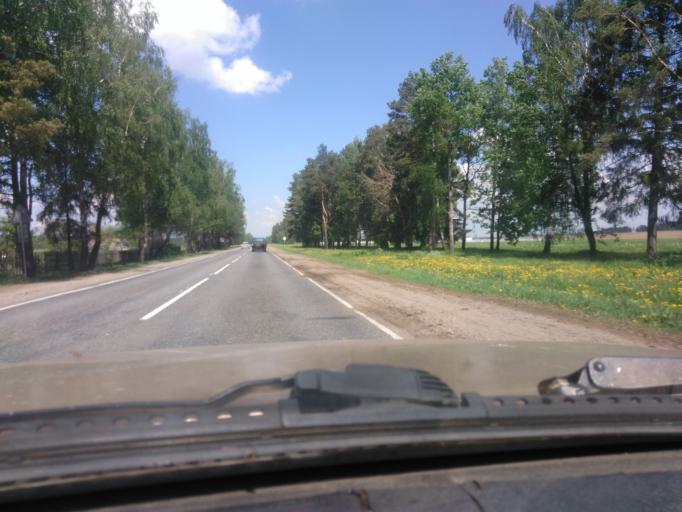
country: BY
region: Mogilev
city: Palykavichy Pyershyya
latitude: 53.9895
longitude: 30.3185
